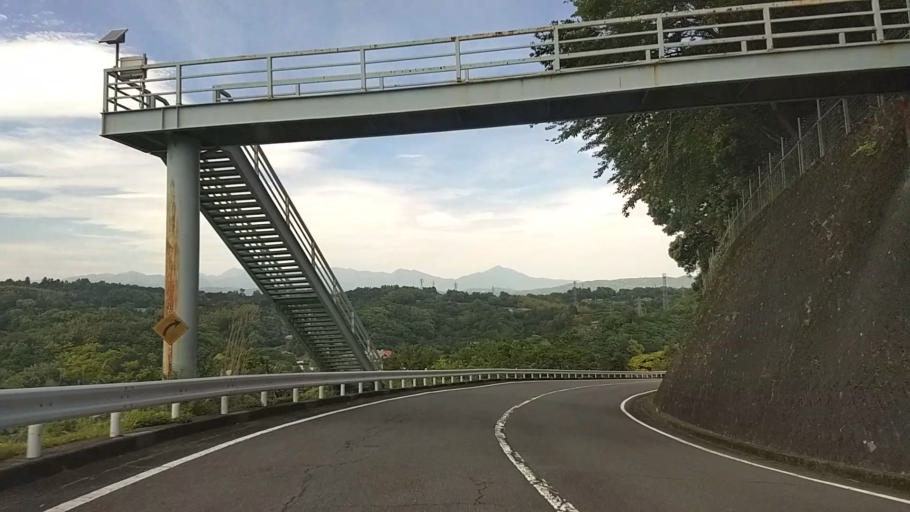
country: JP
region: Kanagawa
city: Odawara
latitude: 35.2419
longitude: 139.1296
